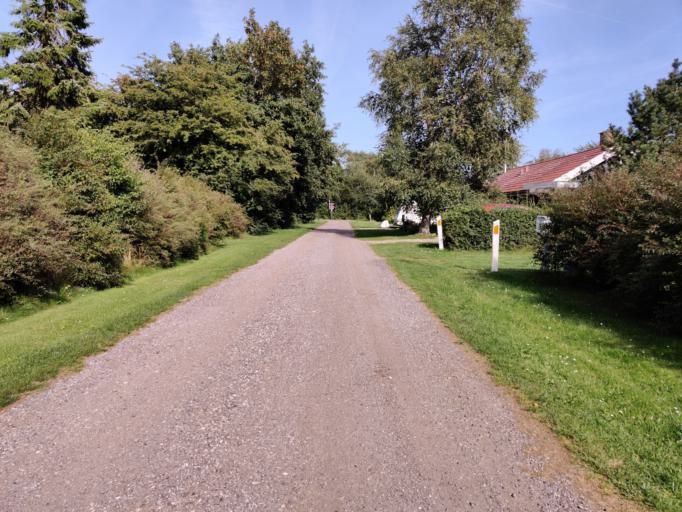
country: DK
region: Zealand
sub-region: Guldborgsund Kommune
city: Nykobing Falster
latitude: 54.5886
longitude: 11.9680
